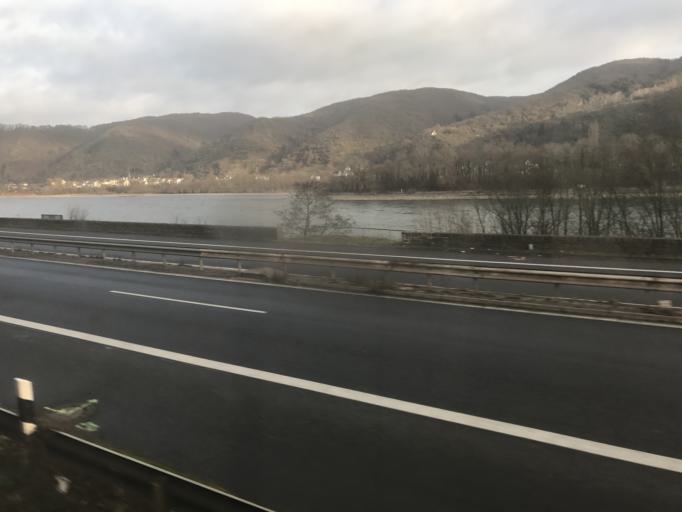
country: DE
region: Rheinland-Pfalz
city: Hammerstein
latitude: 50.4689
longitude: 7.3473
